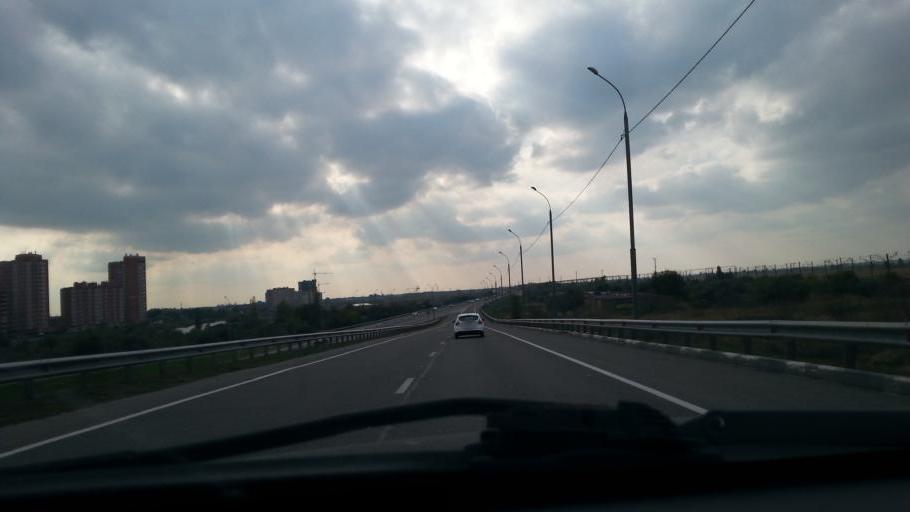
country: RU
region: Rostov
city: Bataysk
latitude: 47.1586
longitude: 39.7352
